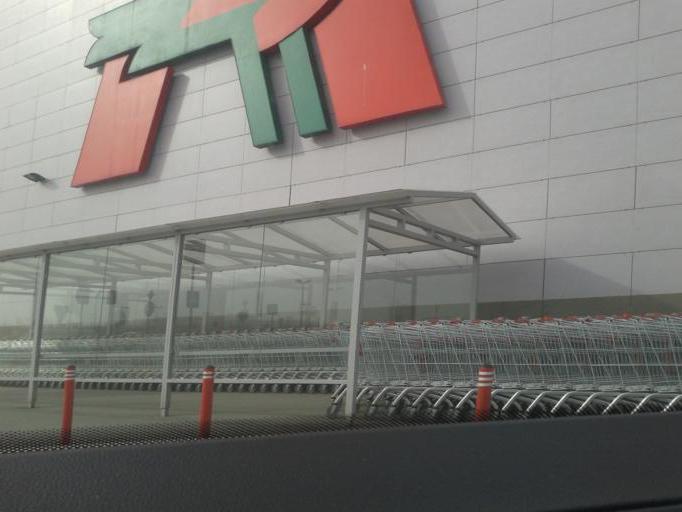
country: RU
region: Volgograd
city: Volgograd
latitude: 48.6352
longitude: 44.4349
